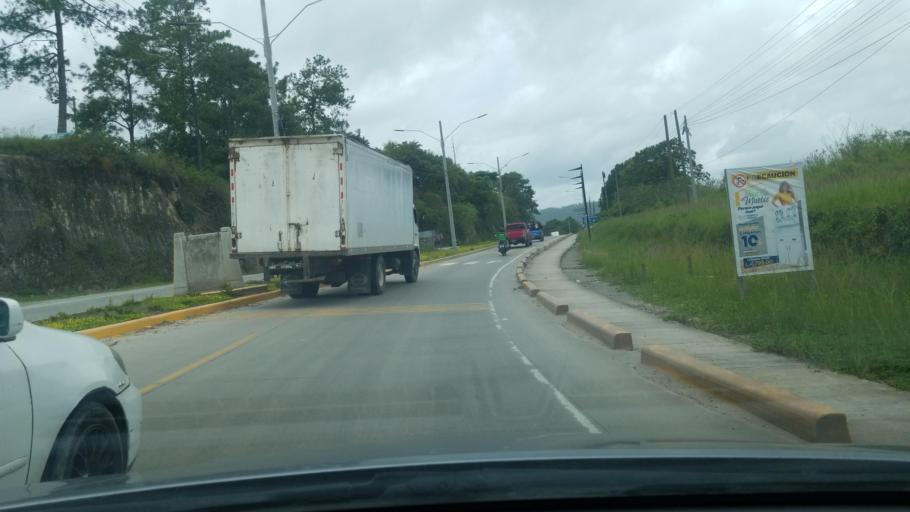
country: HN
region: Copan
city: Santa Rosa de Copan
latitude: 14.7966
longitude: -88.7781
